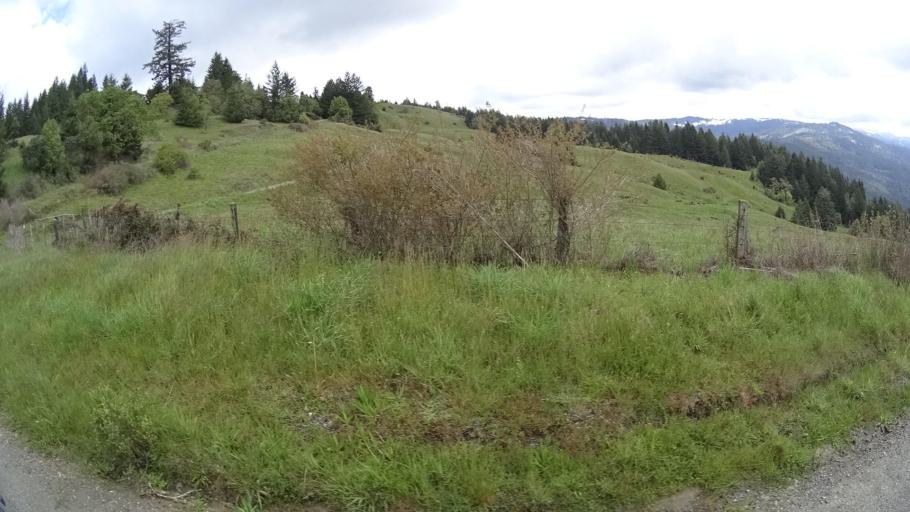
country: US
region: California
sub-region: Humboldt County
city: Blue Lake
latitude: 40.8553
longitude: -123.9175
